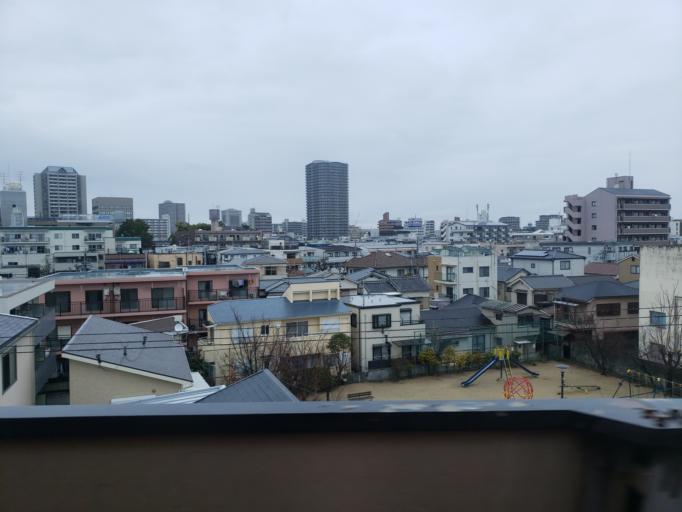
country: JP
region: Hyogo
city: Nishinomiya-hama
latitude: 34.7338
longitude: 135.3480
